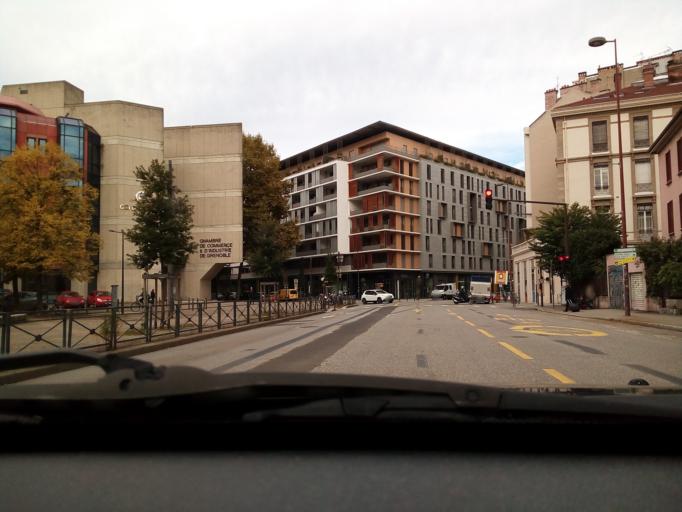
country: FR
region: Rhone-Alpes
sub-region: Departement de l'Isere
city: La Tronche
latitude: 45.1858
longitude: 5.7297
